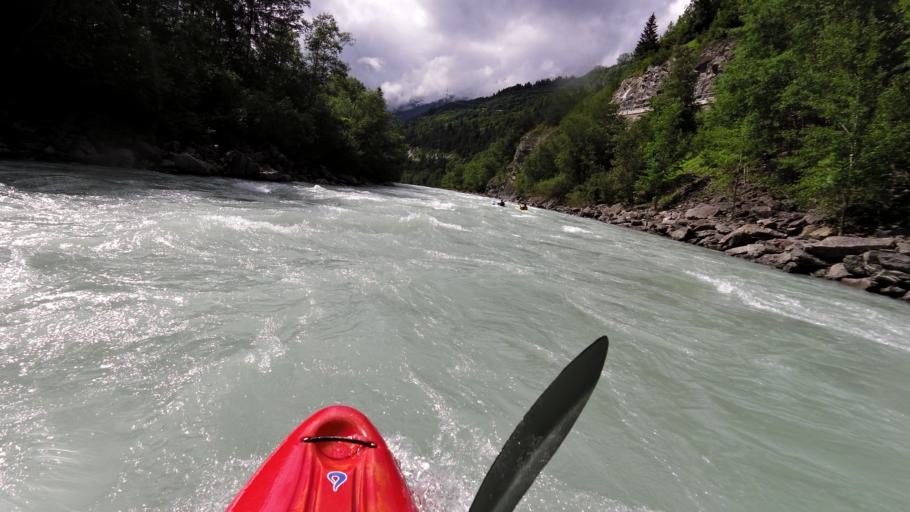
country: AT
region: Tyrol
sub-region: Politischer Bezirk Landeck
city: Zams
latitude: 47.1204
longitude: 10.6020
